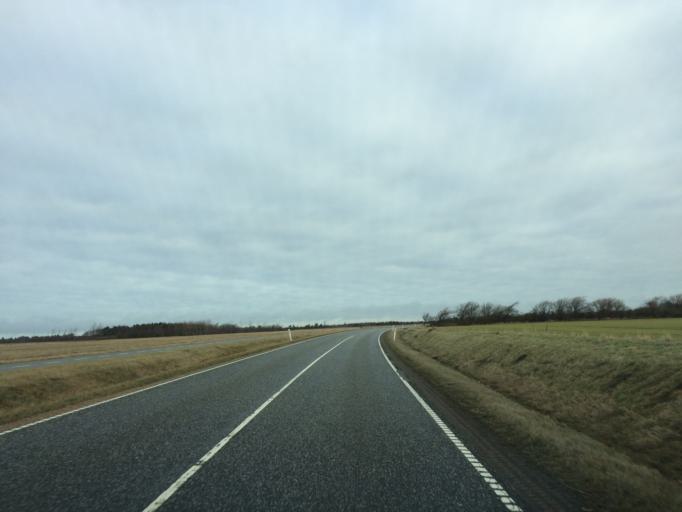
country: DK
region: Central Jutland
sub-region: Holstebro Kommune
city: Ulfborg
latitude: 56.3577
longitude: 8.3820
